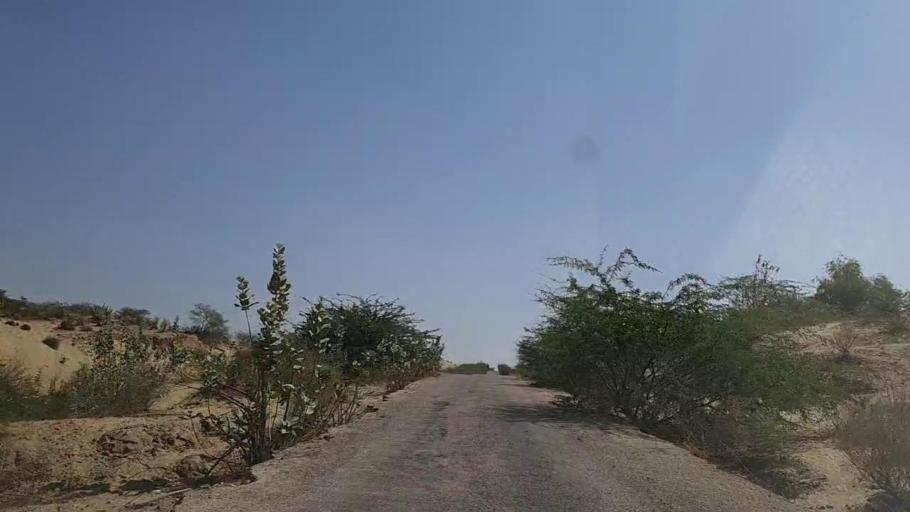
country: PK
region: Sindh
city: Diplo
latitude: 24.4879
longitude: 69.4441
